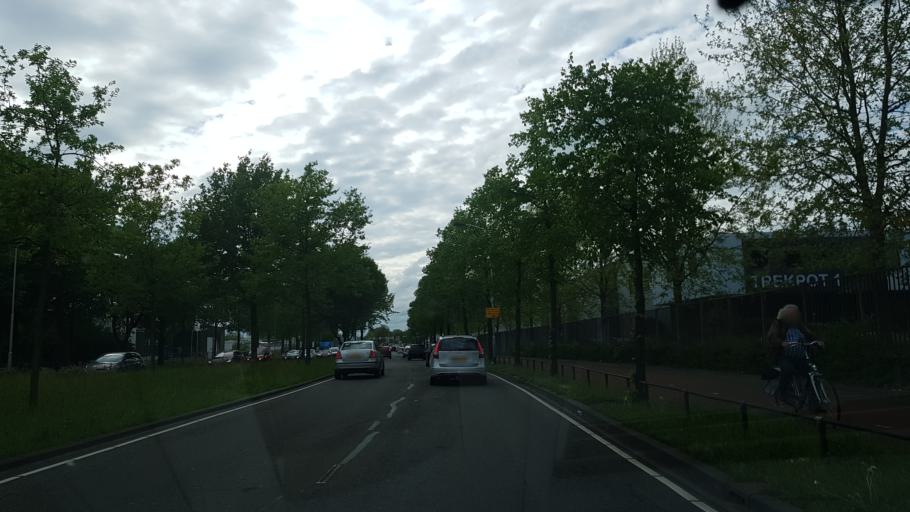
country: NL
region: North Brabant
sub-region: Gemeente Breda
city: Breda
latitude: 51.6019
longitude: 4.7752
